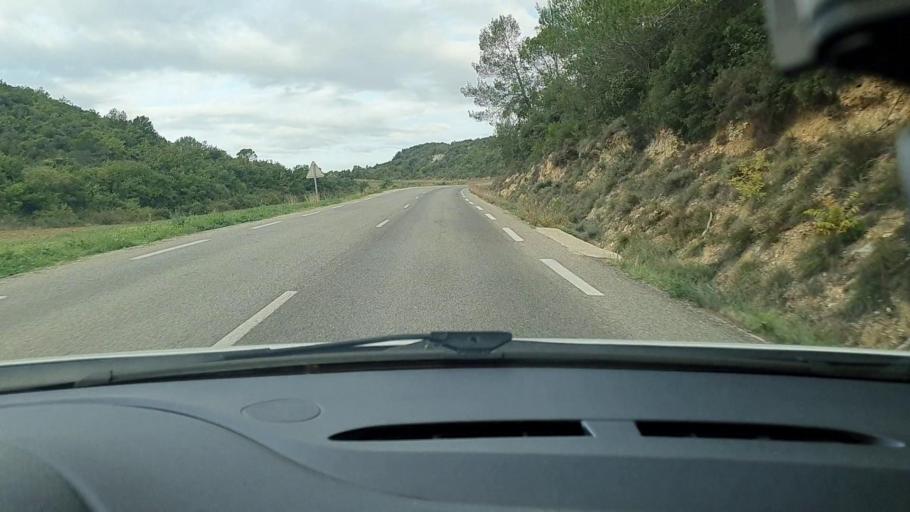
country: FR
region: Languedoc-Roussillon
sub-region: Departement du Gard
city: Mons
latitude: 44.1233
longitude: 4.2339
